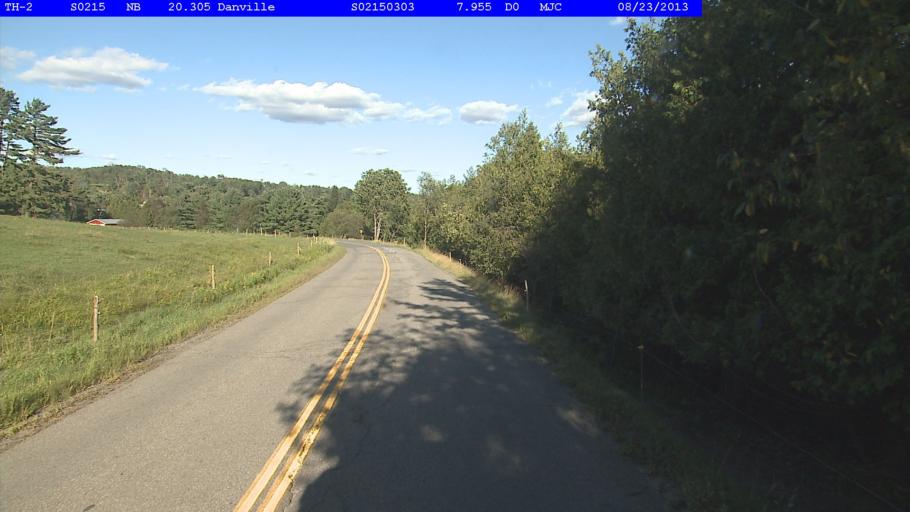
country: US
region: Vermont
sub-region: Caledonia County
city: St Johnsbury
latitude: 44.4578
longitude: -72.1016
